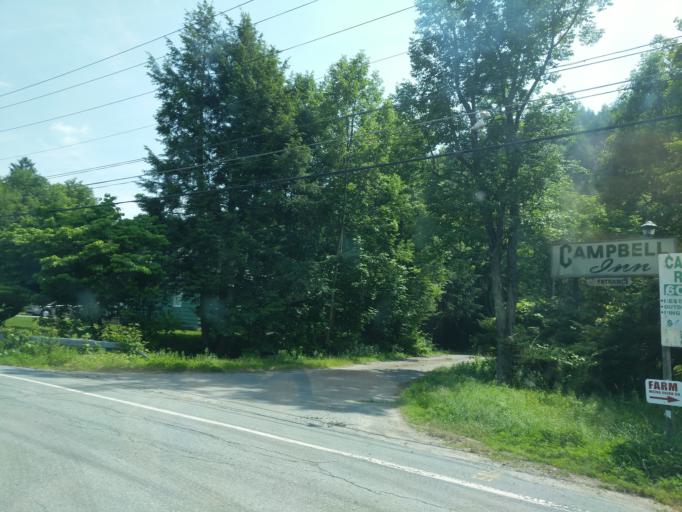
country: US
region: New York
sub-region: Sullivan County
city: Livingston Manor
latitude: 41.9295
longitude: -74.9155
